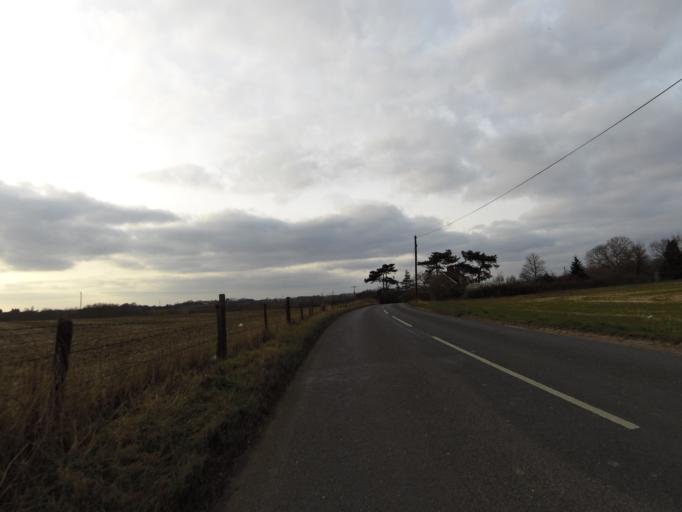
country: GB
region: England
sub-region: Suffolk
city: Ipswich
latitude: 52.0982
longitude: 1.1533
